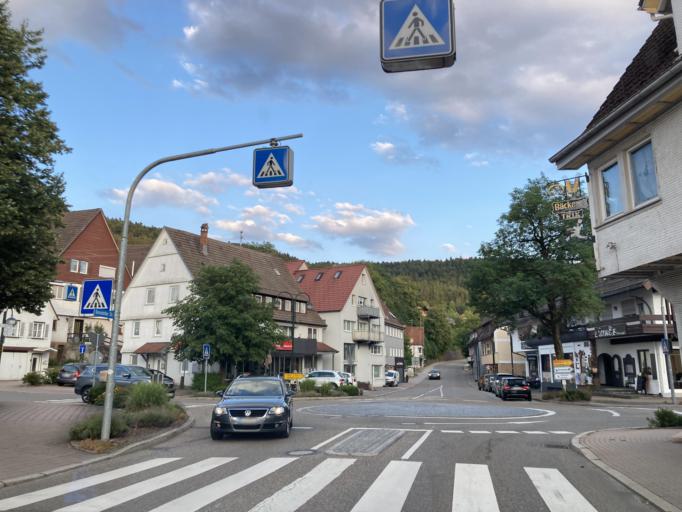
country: DE
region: Baden-Wuerttemberg
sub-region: Karlsruhe Region
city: Glatten
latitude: 48.4442
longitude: 8.5131
